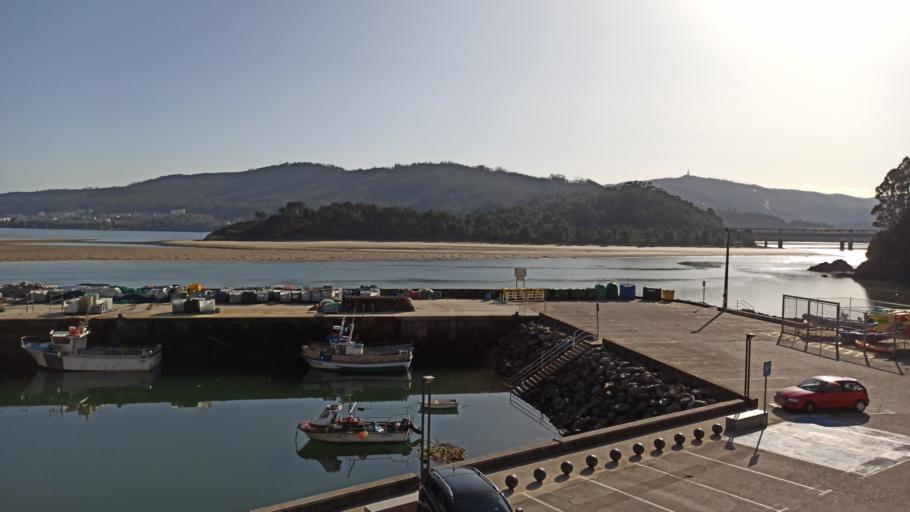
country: ES
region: Galicia
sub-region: Provincia da Coruna
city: Manon
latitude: 43.7372
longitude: -7.7014
